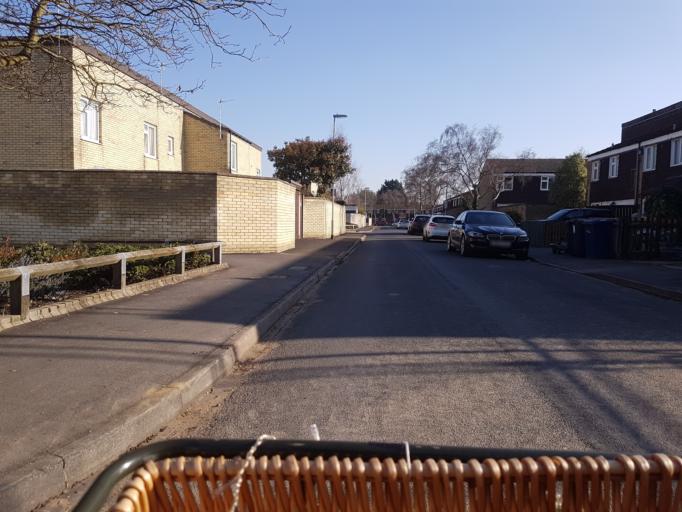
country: GB
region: England
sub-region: Cambridgeshire
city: Histon
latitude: 52.2310
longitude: 0.1317
